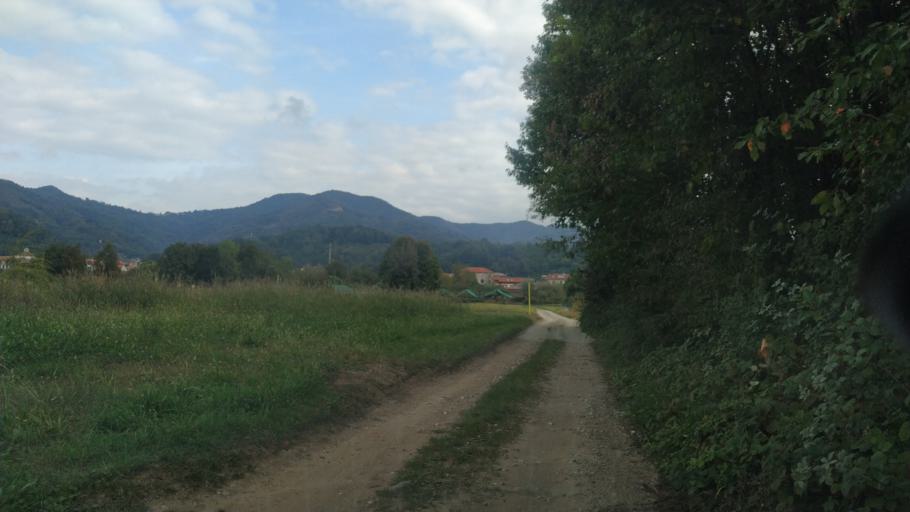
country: IT
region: Piedmont
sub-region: Provincia di Novara
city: Grignasco
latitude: 45.6775
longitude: 8.3346
